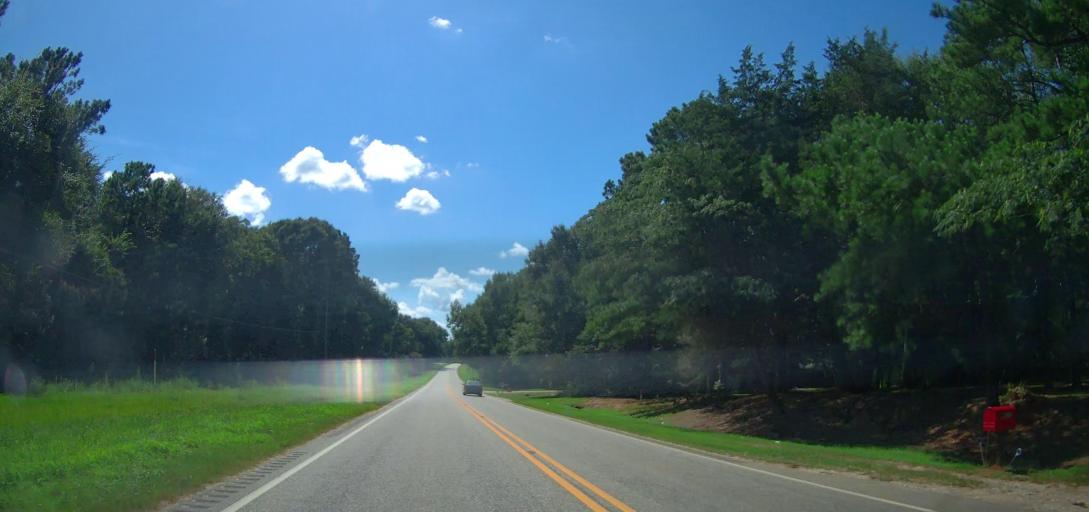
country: US
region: Alabama
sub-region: Elmore County
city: Tallassee
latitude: 32.3789
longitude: -85.8648
